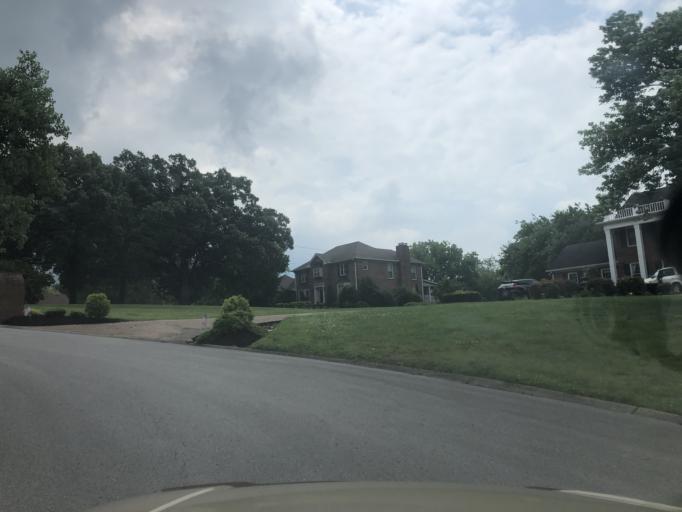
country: US
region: Tennessee
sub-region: Davidson County
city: Lakewood
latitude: 36.2421
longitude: -86.6116
